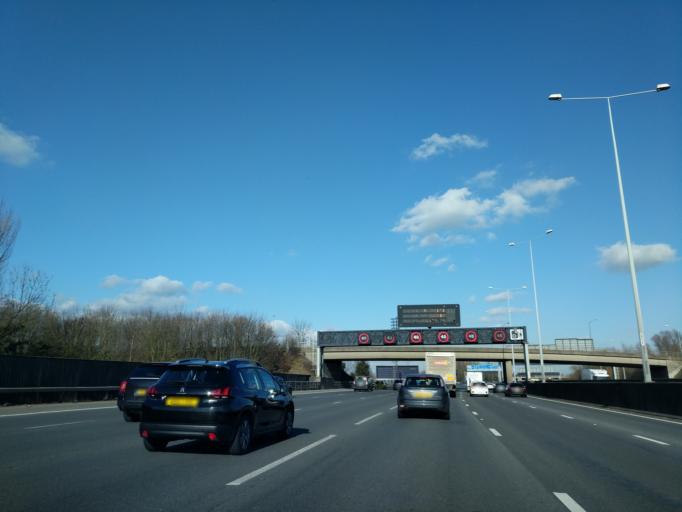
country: GB
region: England
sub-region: Surrey
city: Colnbrook
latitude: 51.4782
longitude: -0.5040
